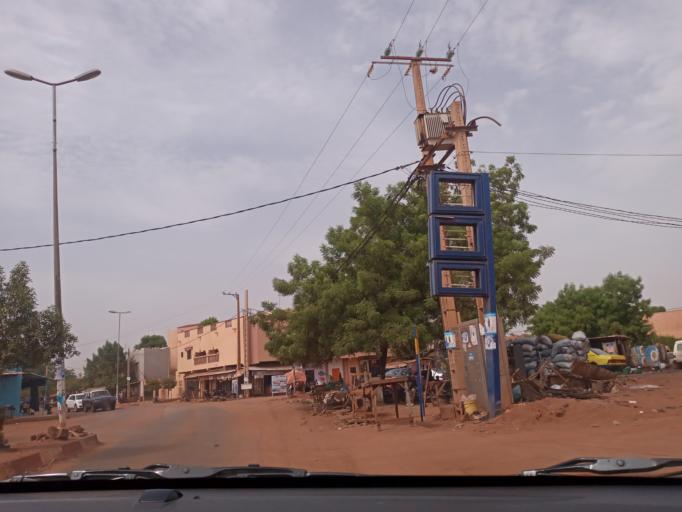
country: ML
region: Bamako
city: Bamako
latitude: 12.6795
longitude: -7.9233
